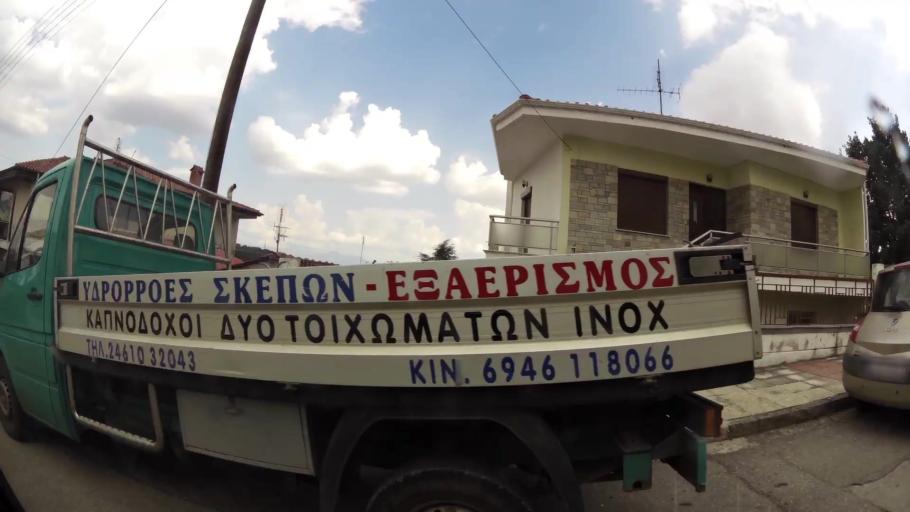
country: GR
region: West Macedonia
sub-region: Nomos Kozanis
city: Koila
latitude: 40.3258
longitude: 21.8247
